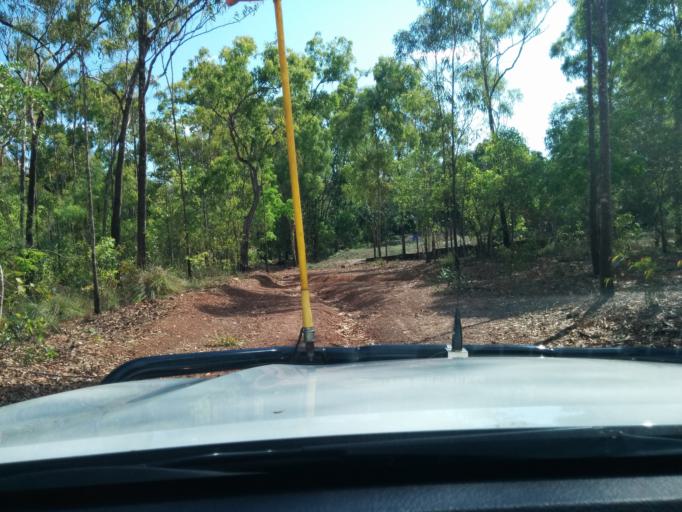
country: AU
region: Northern Territory
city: Alyangula
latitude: -13.8460
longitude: 136.4193
